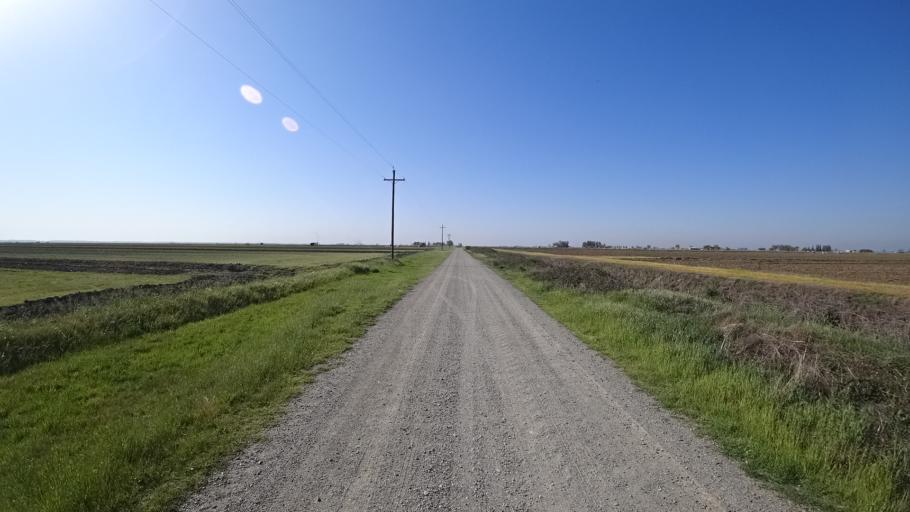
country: US
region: California
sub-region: Glenn County
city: Willows
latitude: 39.5532
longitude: -122.0840
